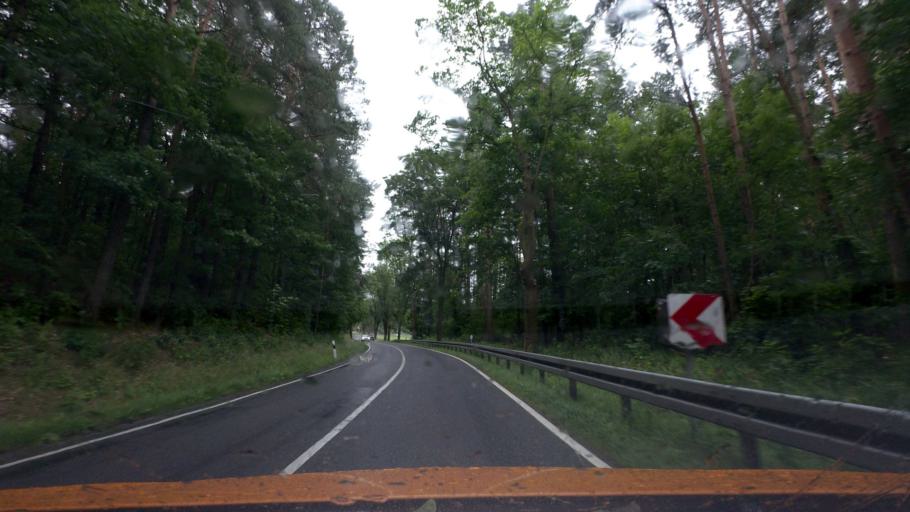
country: DE
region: Brandenburg
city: Strausberg
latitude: 52.5978
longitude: 13.8882
